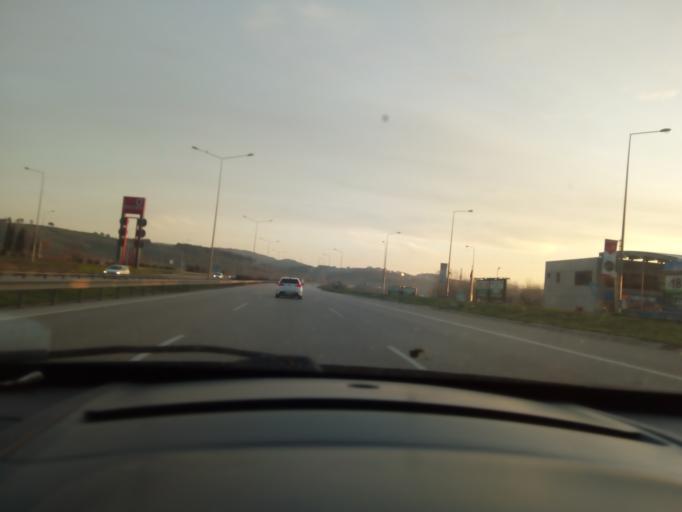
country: TR
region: Bursa
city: Niluefer
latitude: 40.2825
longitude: 28.9960
